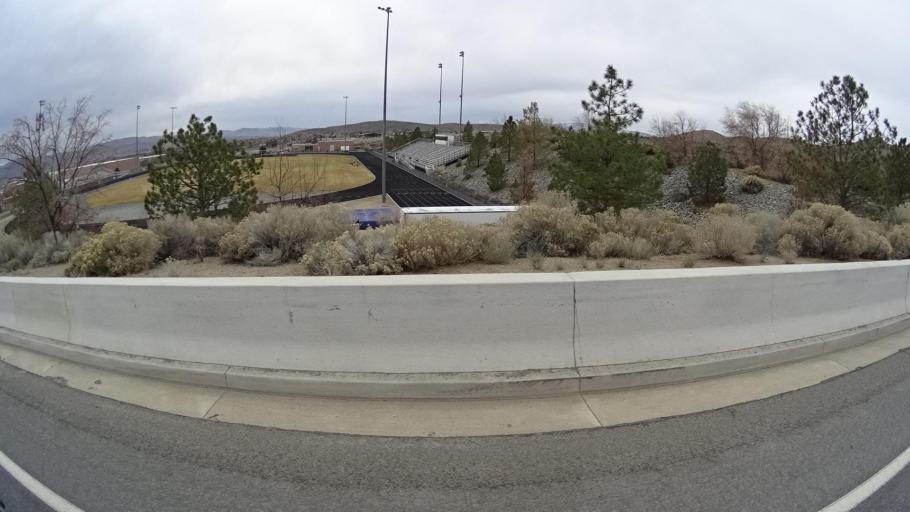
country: US
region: Nevada
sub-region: Washoe County
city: Spanish Springs
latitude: 39.6529
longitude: -119.7324
